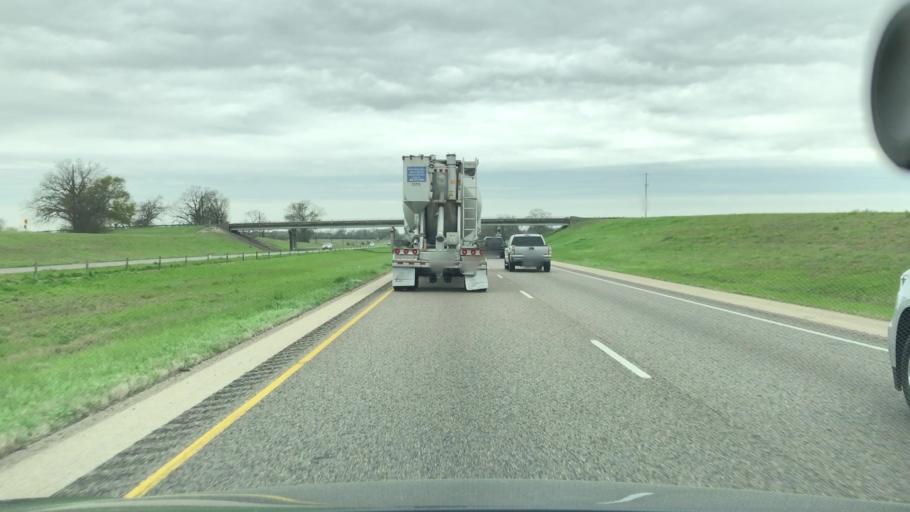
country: US
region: Texas
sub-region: Madison County
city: Madisonville
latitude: 31.0466
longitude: -95.9455
